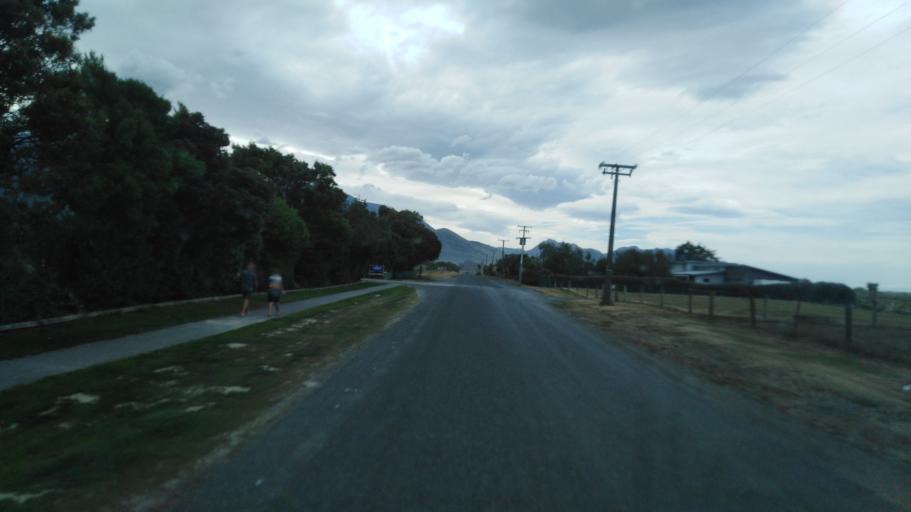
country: NZ
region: Canterbury
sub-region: Kaikoura District
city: Kaikoura
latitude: -42.3749
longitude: 173.6821
